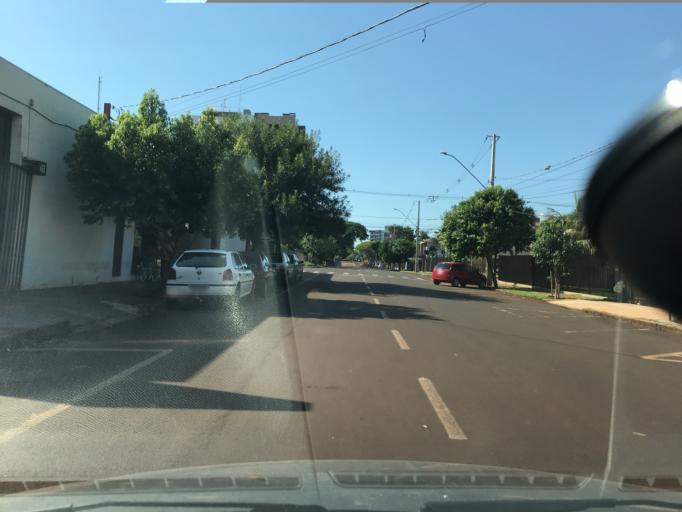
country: BR
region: Parana
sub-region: Palotina
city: Palotina
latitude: -24.2819
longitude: -53.8417
